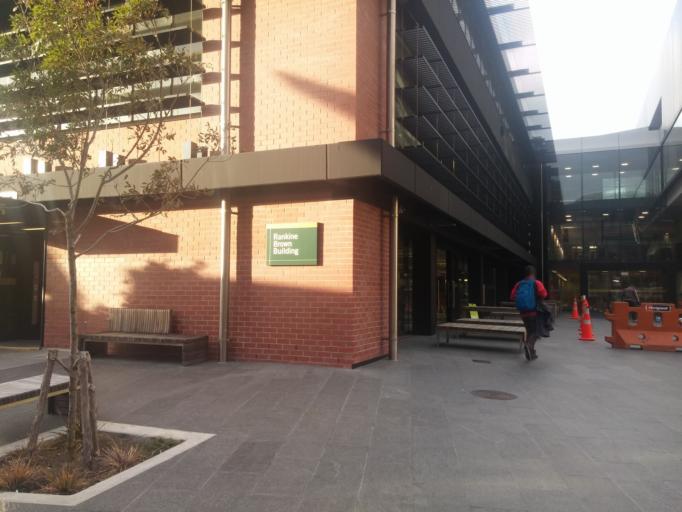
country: NZ
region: Wellington
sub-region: Wellington City
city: Kelburn
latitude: -41.2889
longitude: 174.7688
